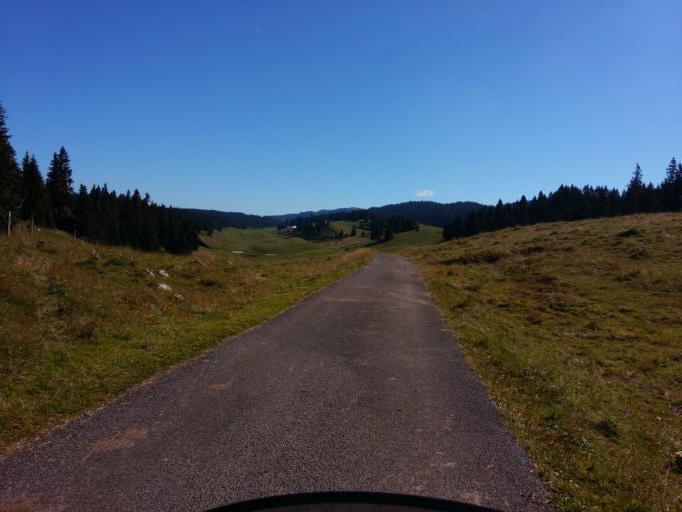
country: CH
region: Vaud
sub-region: Nyon District
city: Saint-George
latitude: 46.5301
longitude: 6.2126
